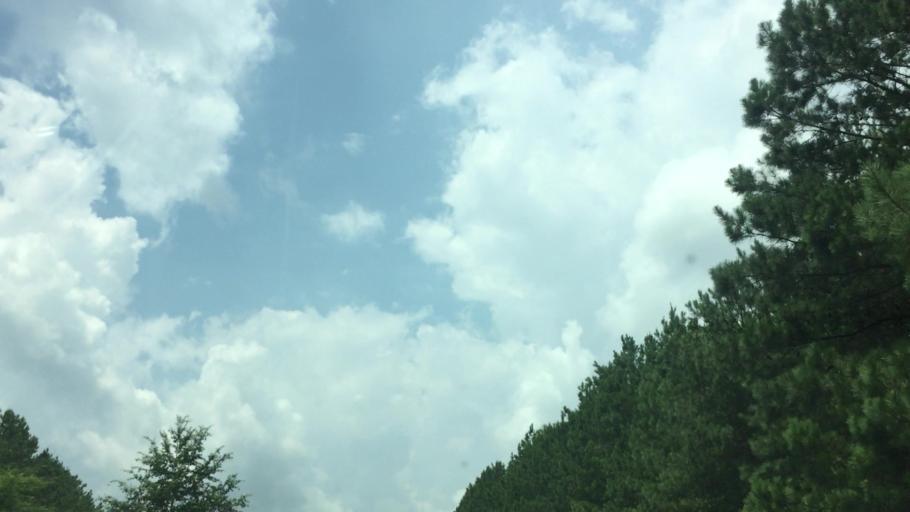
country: US
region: Georgia
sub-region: Fulton County
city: Union City
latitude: 33.6244
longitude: -84.5824
